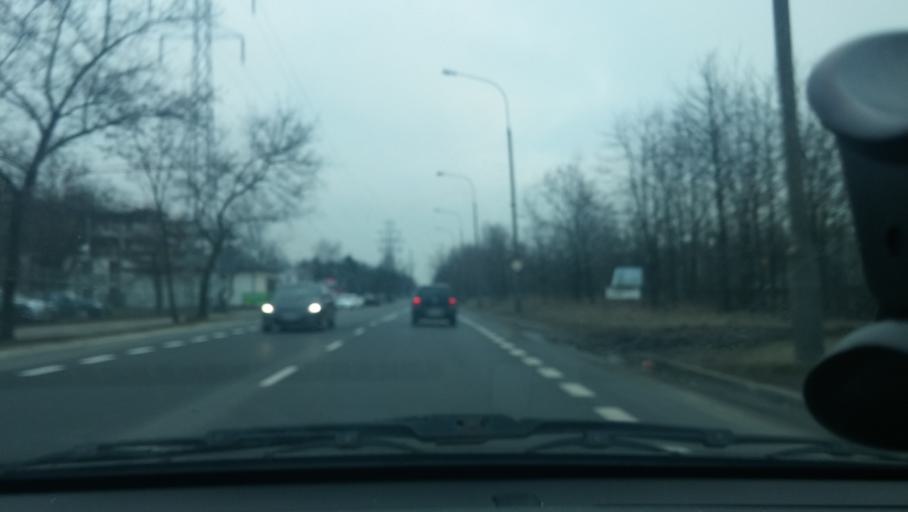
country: PL
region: Masovian Voivodeship
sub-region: Warszawa
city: Wawer
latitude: 52.2131
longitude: 21.1603
